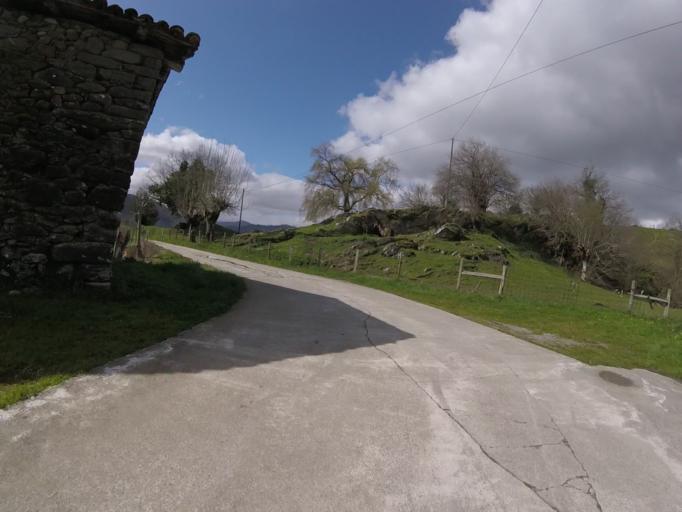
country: ES
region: Basque Country
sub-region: Provincia de Guipuzcoa
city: Albiztur
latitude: 43.1400
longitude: -2.1268
